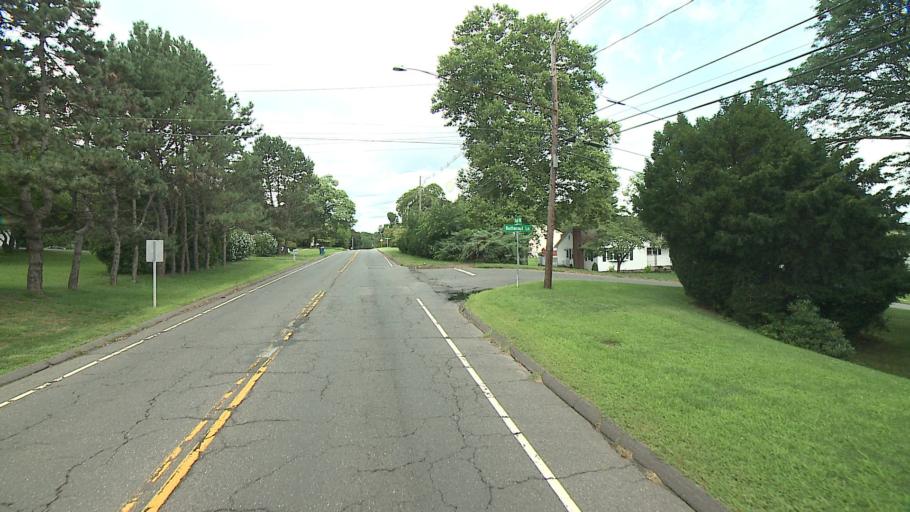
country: US
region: Connecticut
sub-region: Hartford County
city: Kensington
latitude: 41.6383
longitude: -72.7885
